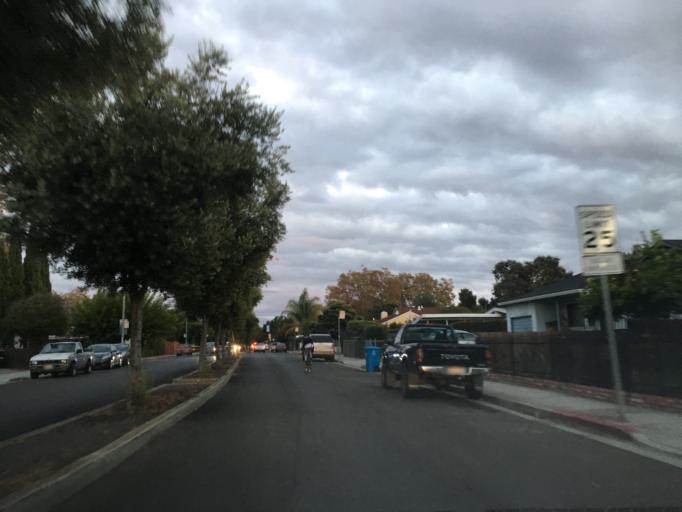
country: US
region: California
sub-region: San Mateo County
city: East Palo Alto
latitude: 37.4725
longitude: -122.1536
